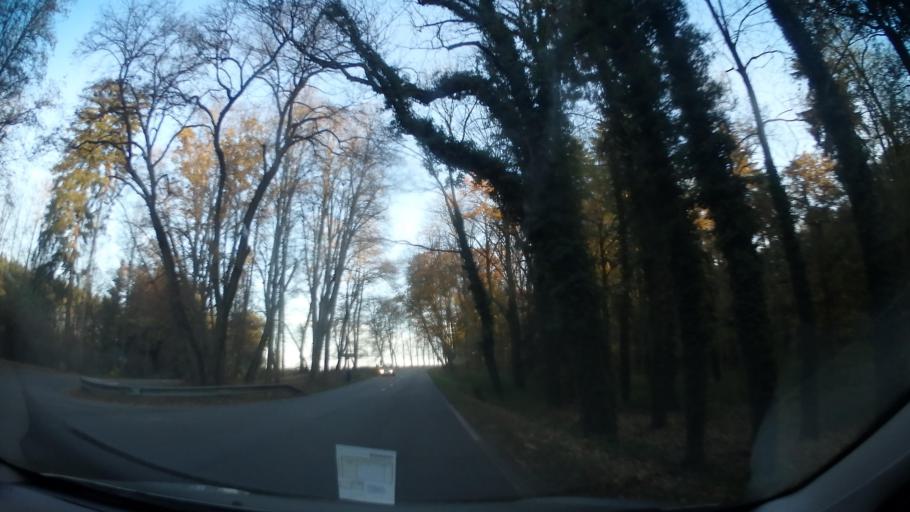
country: CZ
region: Central Bohemia
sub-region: Okres Benesov
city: Benesov
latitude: 49.7815
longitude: 14.6637
